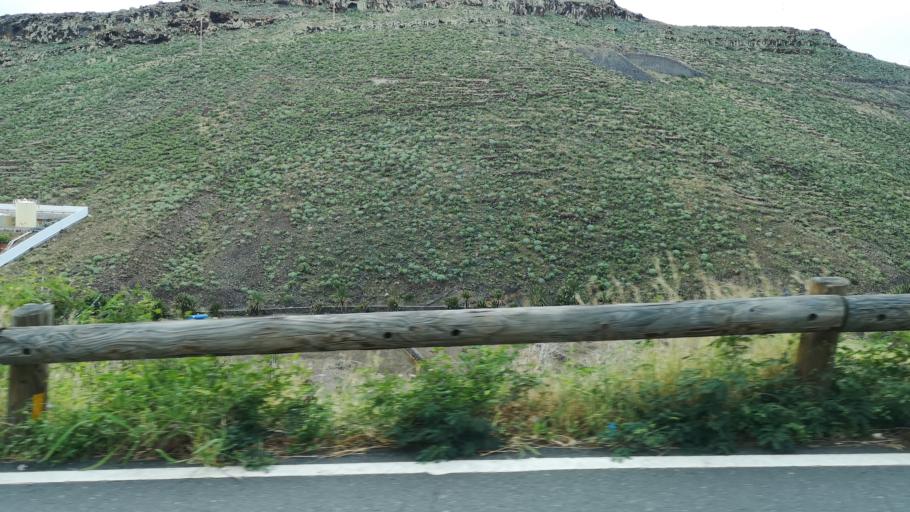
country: ES
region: Canary Islands
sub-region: Provincia de Santa Cruz de Tenerife
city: San Sebastian de la Gomera
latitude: 28.0902
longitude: -17.1198
